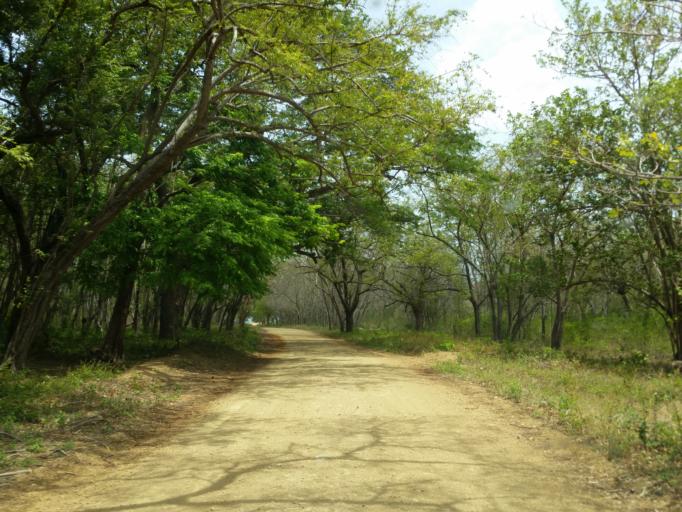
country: NI
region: Rivas
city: Tola
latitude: 11.4171
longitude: -86.0586
